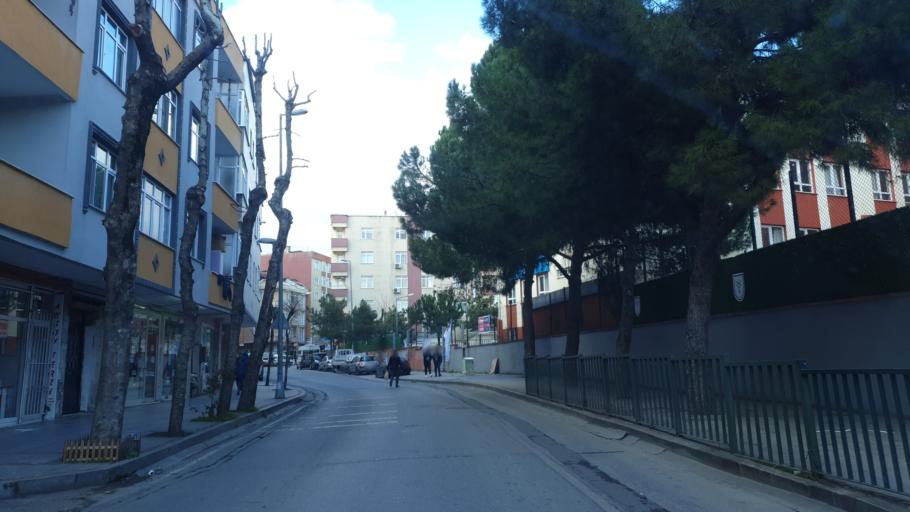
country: TR
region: Istanbul
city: Pendik
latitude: 40.8740
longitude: 29.2727
